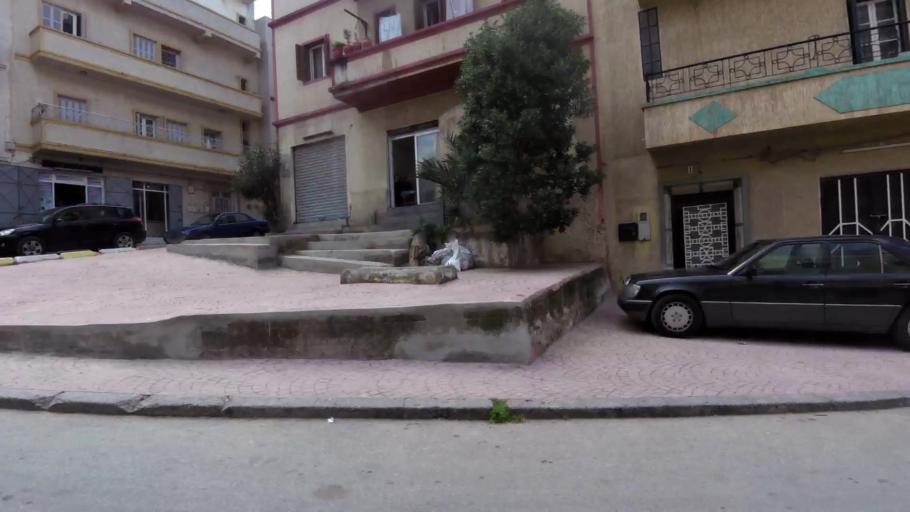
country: MA
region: Tanger-Tetouan
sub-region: Tanger-Assilah
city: Tangier
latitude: 35.7603
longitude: -5.8142
